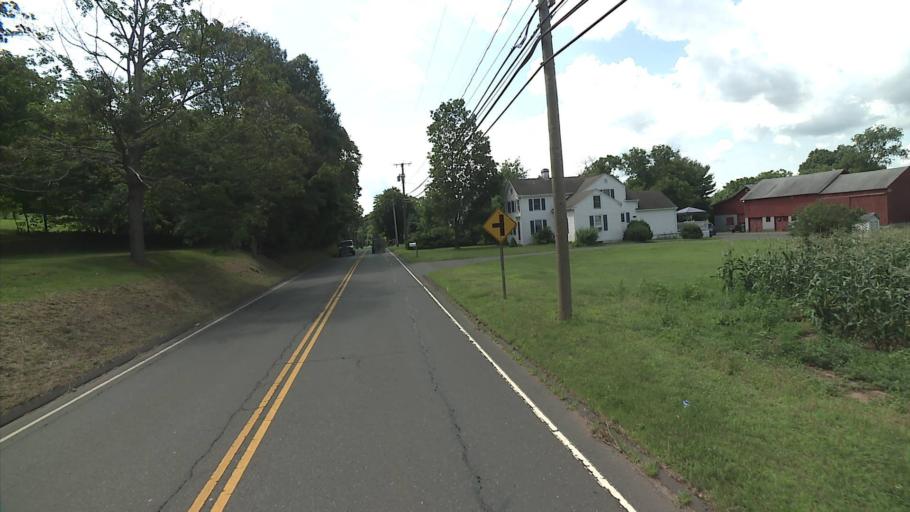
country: US
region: Connecticut
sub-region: Hartford County
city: Glastonbury Center
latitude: 41.6541
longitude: -72.6040
